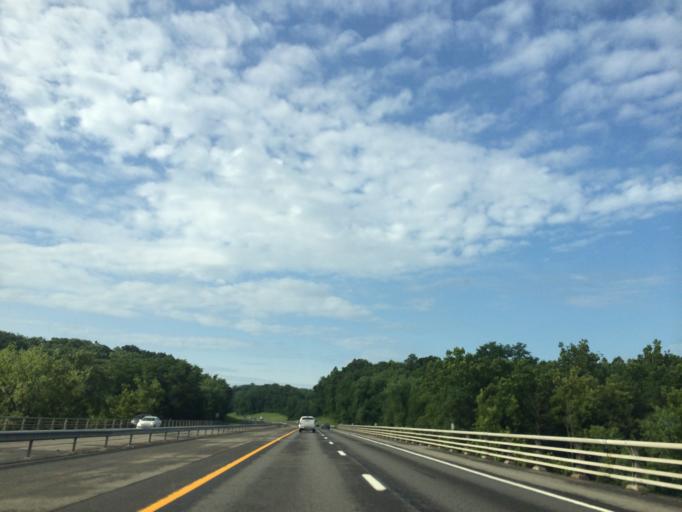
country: US
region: New York
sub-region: Ulster County
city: Rosendale Village
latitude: 41.8533
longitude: -74.0593
